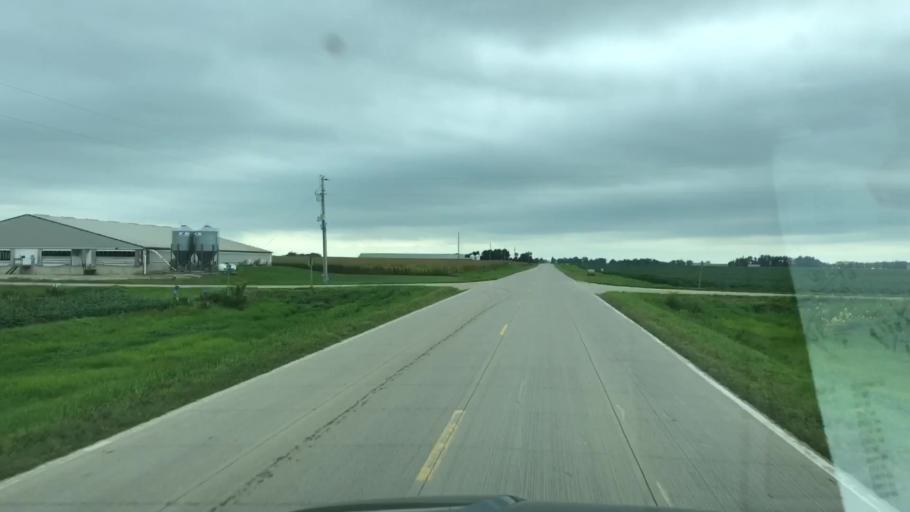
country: US
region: Iowa
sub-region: O'Brien County
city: Sheldon
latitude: 43.1286
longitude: -95.9799
